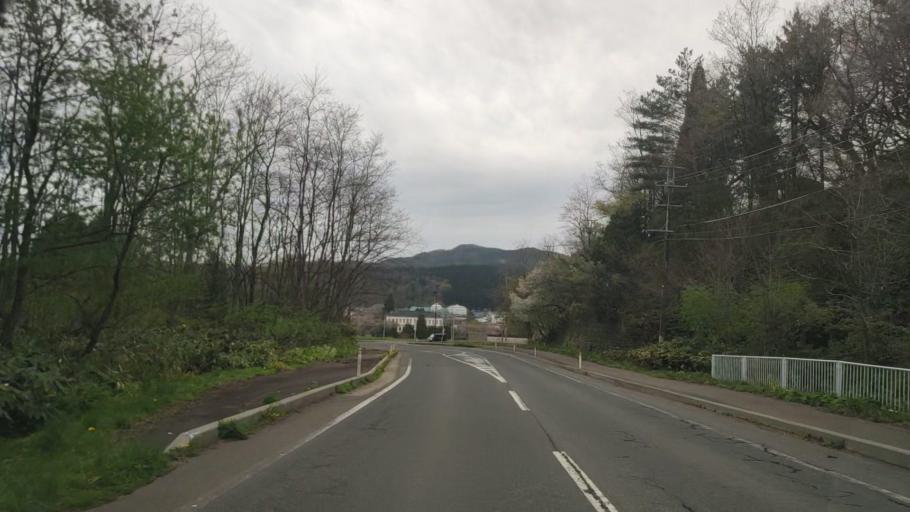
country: JP
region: Akita
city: Hanawa
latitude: 40.3297
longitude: 140.7485
